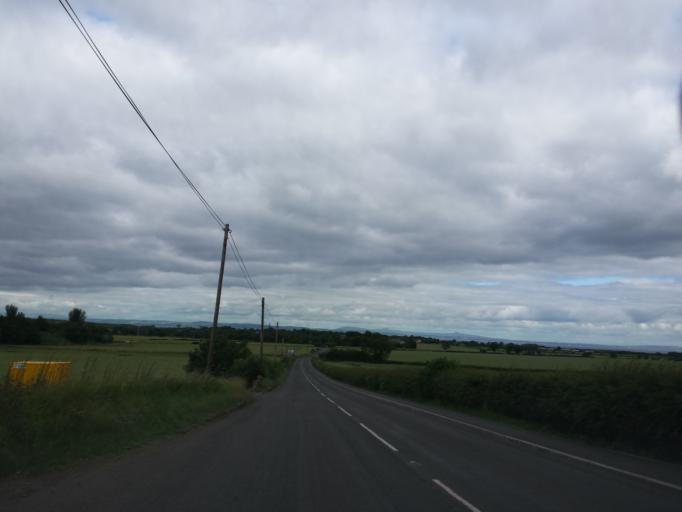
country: GB
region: Scotland
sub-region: East Lothian
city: Musselburgh
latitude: 55.9193
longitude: -3.0291
